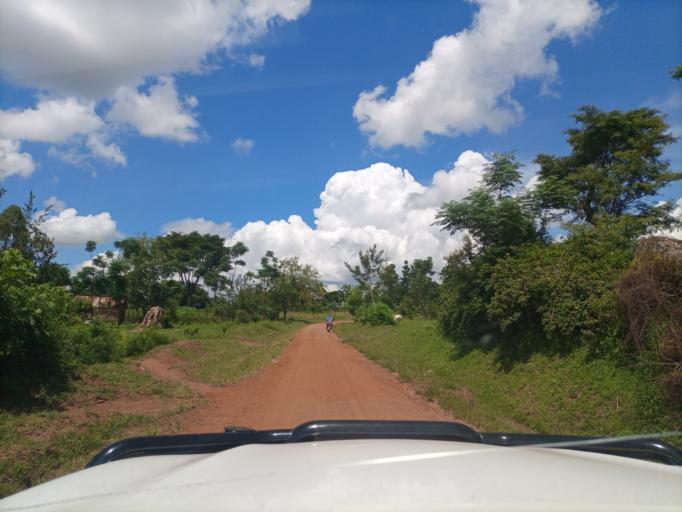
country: UG
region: Eastern Region
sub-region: Tororo District
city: Tororo
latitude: 0.6968
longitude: 34.0119
